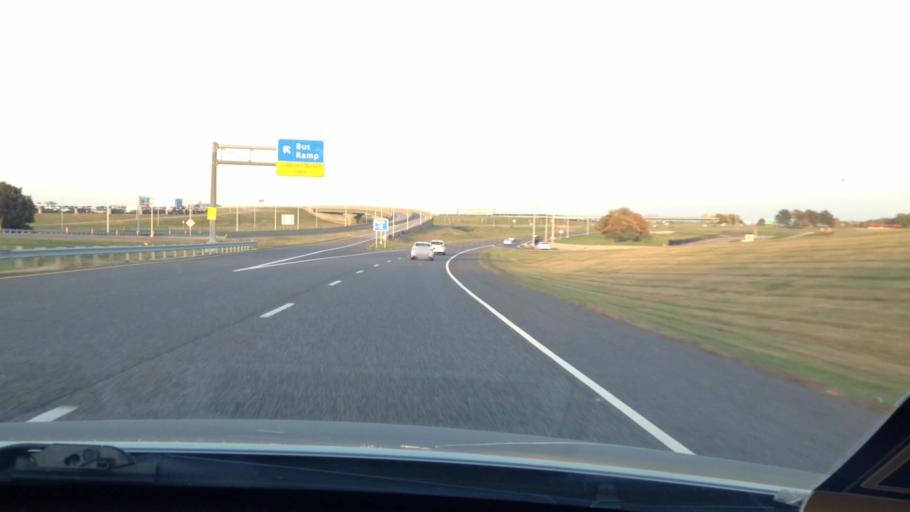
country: US
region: Missouri
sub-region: Platte County
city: Weatherby Lake
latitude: 39.3091
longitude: -94.7062
